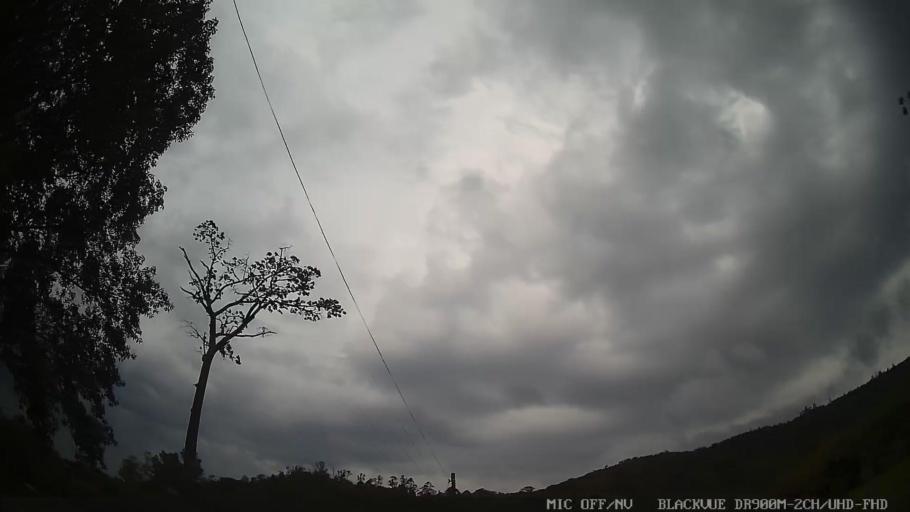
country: BR
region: Sao Paulo
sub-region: Itatiba
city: Itatiba
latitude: -23.0230
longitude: -46.8950
